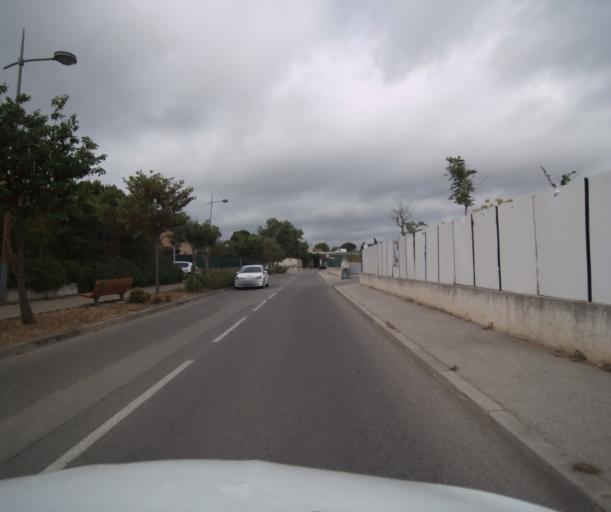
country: FR
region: Provence-Alpes-Cote d'Azur
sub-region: Departement du Var
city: Ollioules
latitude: 43.1235
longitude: 5.8302
